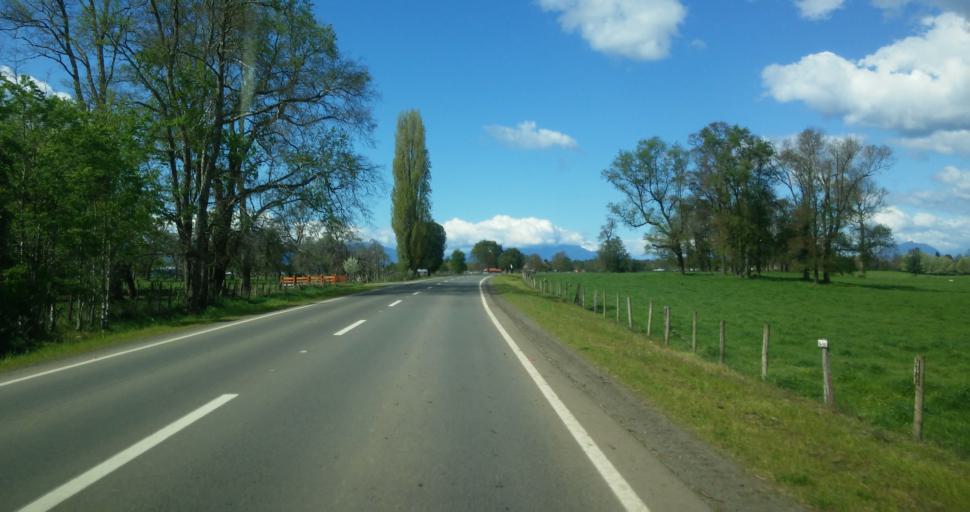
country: CL
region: Los Rios
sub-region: Provincia del Ranco
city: Rio Bueno
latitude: -40.2410
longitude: -72.6064
